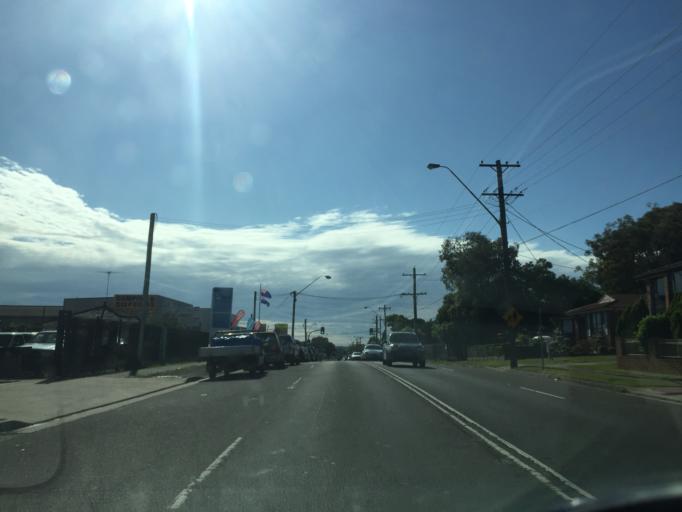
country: AU
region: New South Wales
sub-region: Fairfield
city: Fairfield Heights
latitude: -33.8524
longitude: 150.9330
